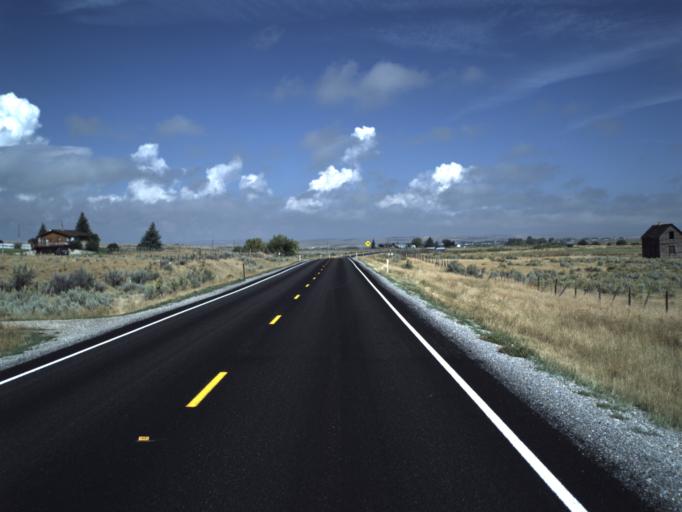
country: US
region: Utah
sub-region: Rich County
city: Randolph
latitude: 41.6069
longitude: -111.1777
